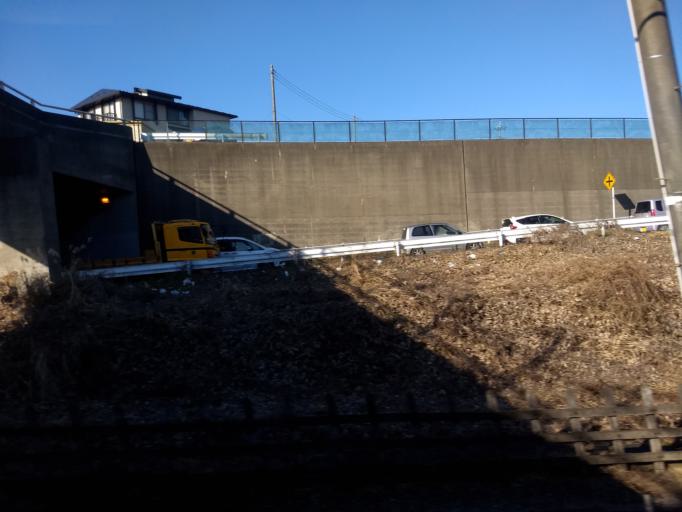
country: JP
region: Chiba
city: Shiroi
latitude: 35.7891
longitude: 140.0915
